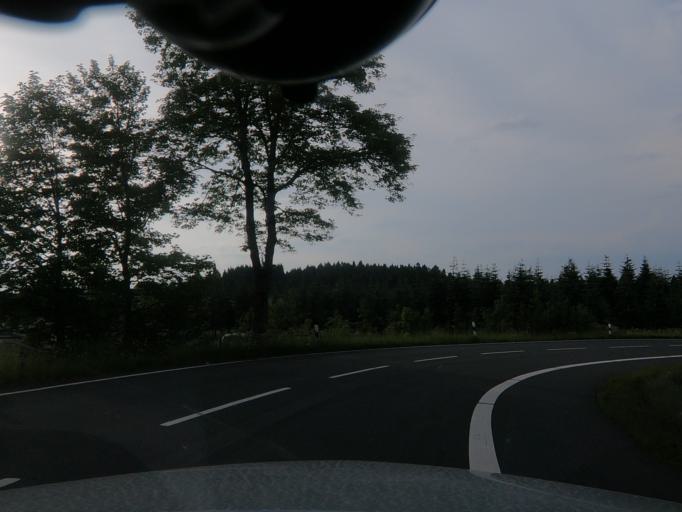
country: DE
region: North Rhine-Westphalia
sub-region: Regierungsbezirk Arnsberg
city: Winterberg
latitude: 51.1839
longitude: 8.4813
